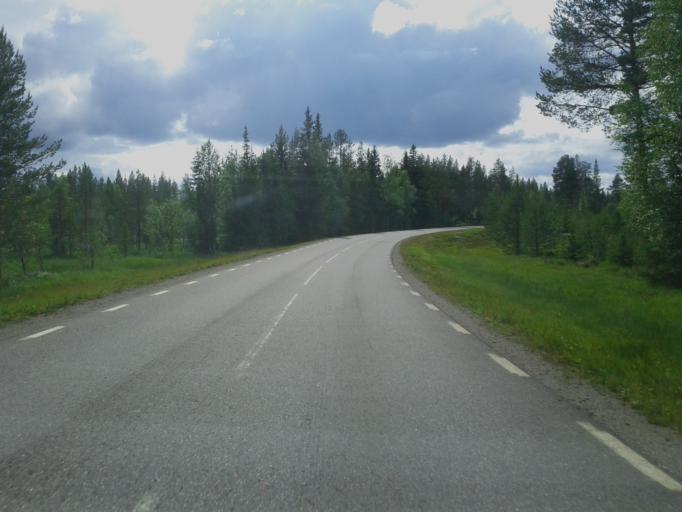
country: SE
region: Vaesterbotten
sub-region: Mala Kommun
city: Mala
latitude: 65.2321
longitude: 18.5743
